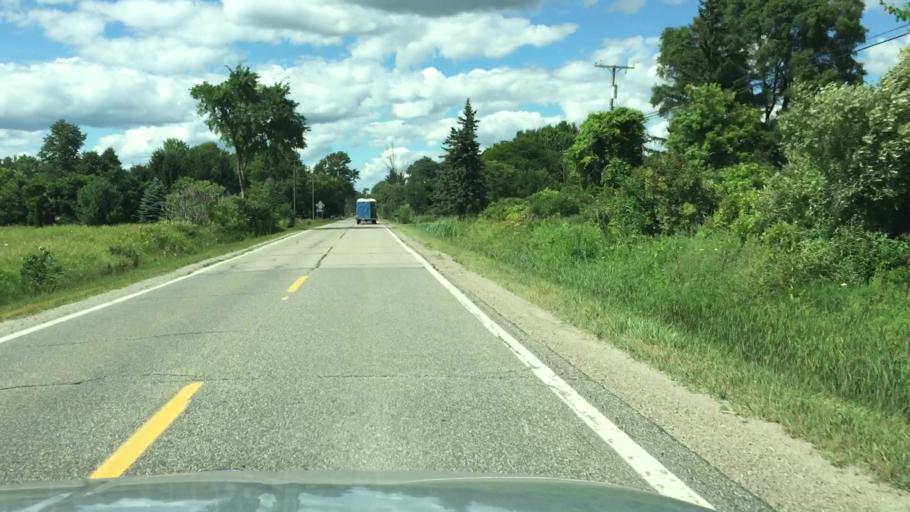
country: US
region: Michigan
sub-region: Macomb County
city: Armada
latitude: 42.8864
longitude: -82.9456
